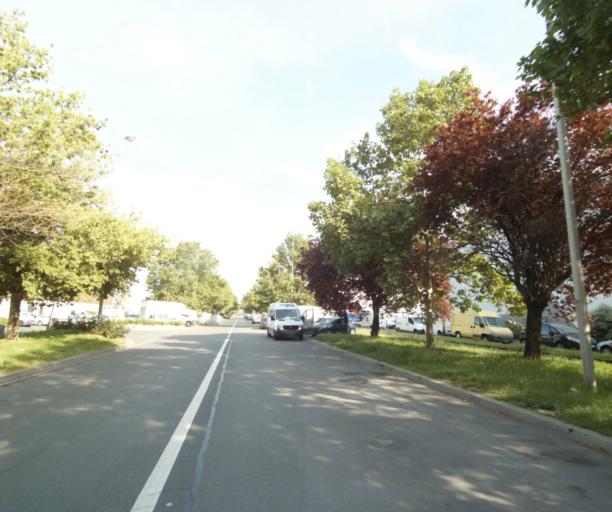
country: FR
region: Ile-de-France
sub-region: Departement des Hauts-de-Seine
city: Bois-Colombes
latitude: 48.9405
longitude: 2.2788
